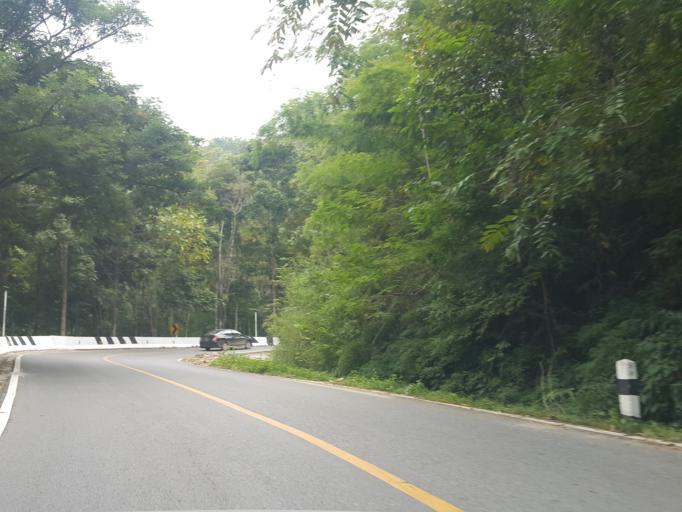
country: TH
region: Mae Hong Son
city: Mae Hi
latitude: 19.2761
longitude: 98.4982
